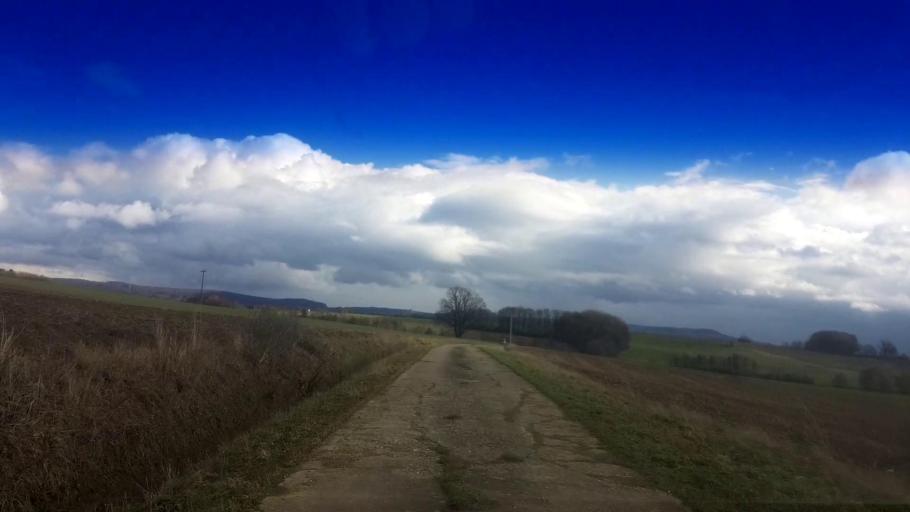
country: DE
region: Bavaria
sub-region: Upper Franconia
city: Schesslitz
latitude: 49.9935
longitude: 11.0163
